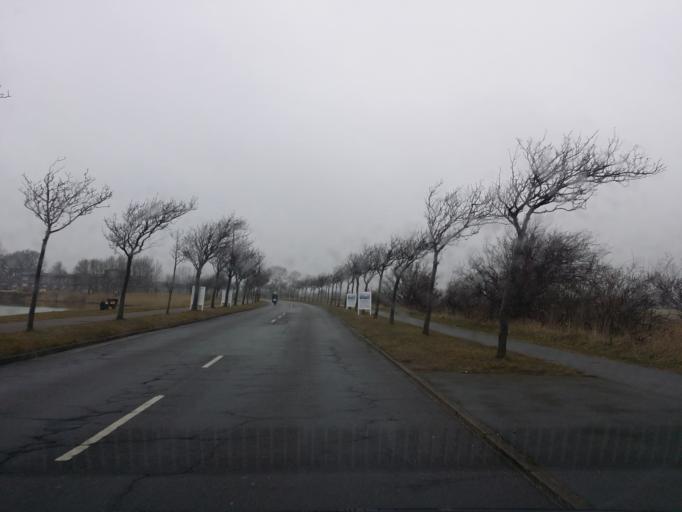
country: DE
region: Schleswig-Holstein
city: Burg auf Fehmarn
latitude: 54.4165
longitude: 11.2116
